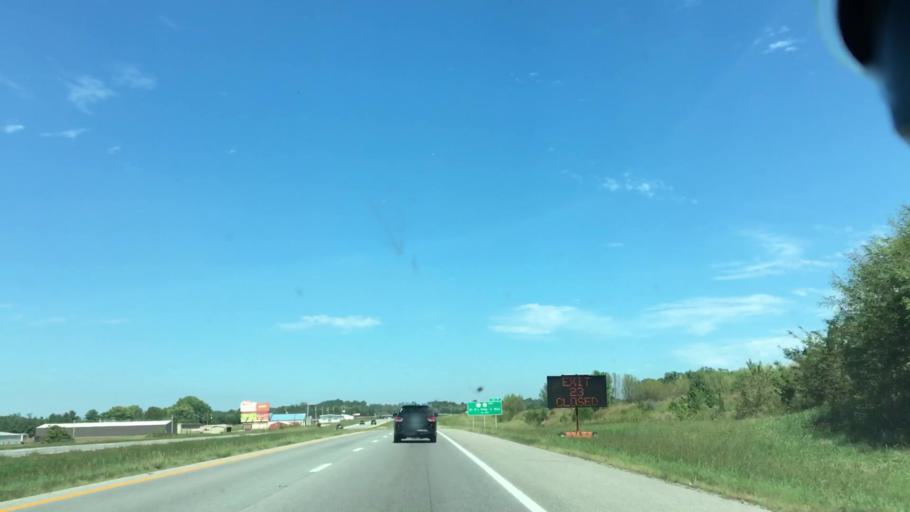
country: US
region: Kentucky
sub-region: Christian County
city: Hopkinsville
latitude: 36.8857
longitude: -87.4687
